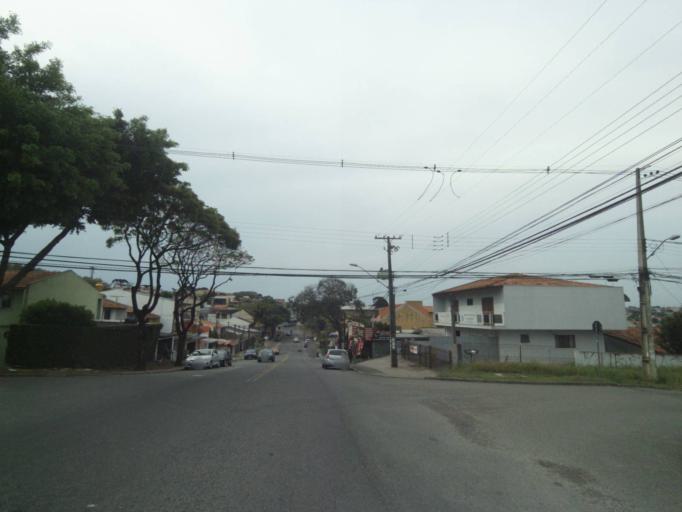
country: BR
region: Parana
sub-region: Pinhais
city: Pinhais
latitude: -25.4153
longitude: -49.2050
